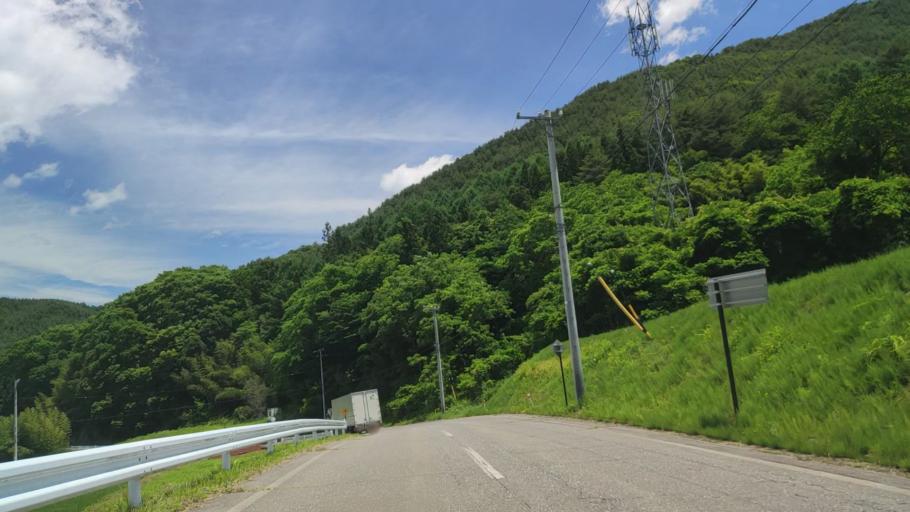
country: JP
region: Nagano
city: Kamimaruko
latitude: 36.2291
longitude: 138.2544
